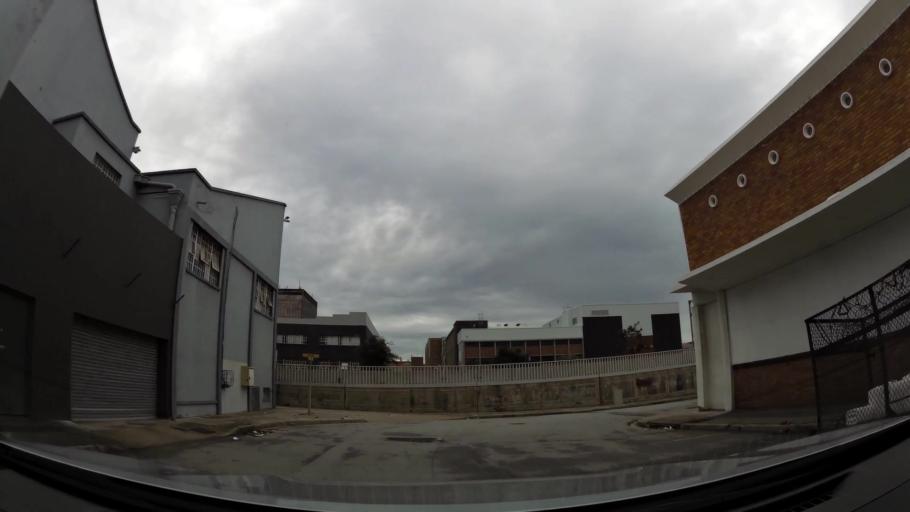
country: ZA
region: Eastern Cape
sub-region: Nelson Mandela Bay Metropolitan Municipality
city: Port Elizabeth
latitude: -33.9469
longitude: 25.6071
